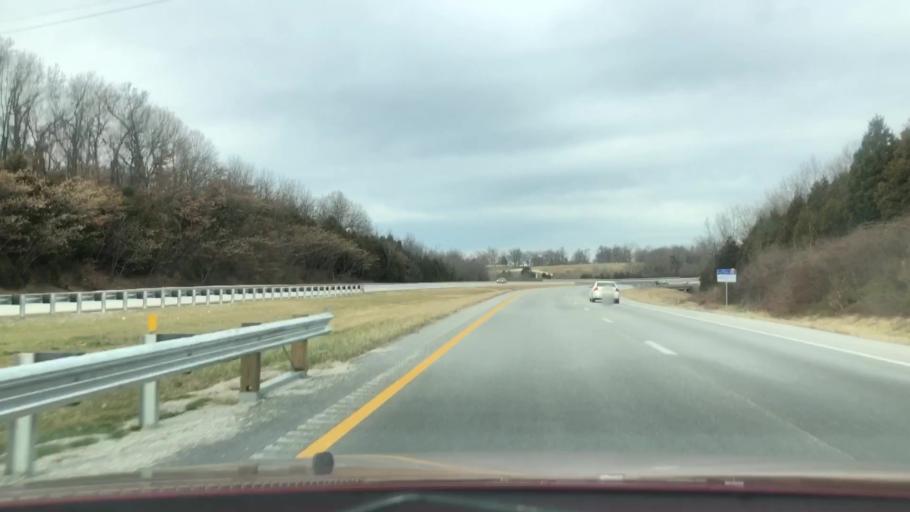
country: US
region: Missouri
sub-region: Greene County
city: Springfield
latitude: 37.2609
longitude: -93.2248
